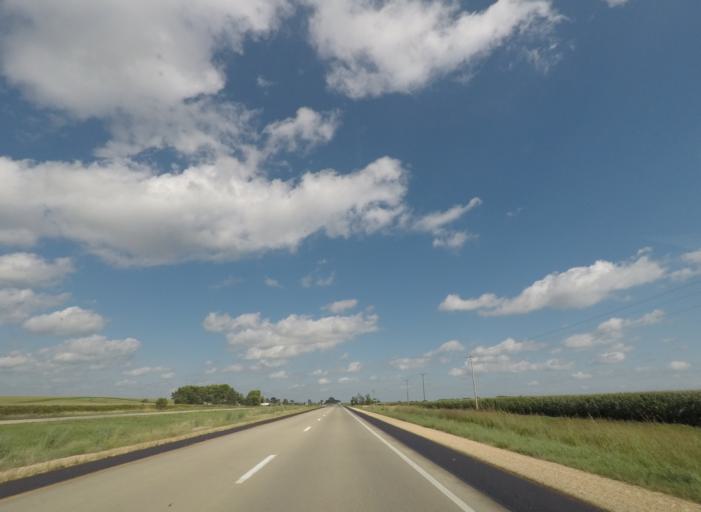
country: US
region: Iowa
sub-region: Dubuque County
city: Cascade
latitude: 42.2855
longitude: -91.0893
